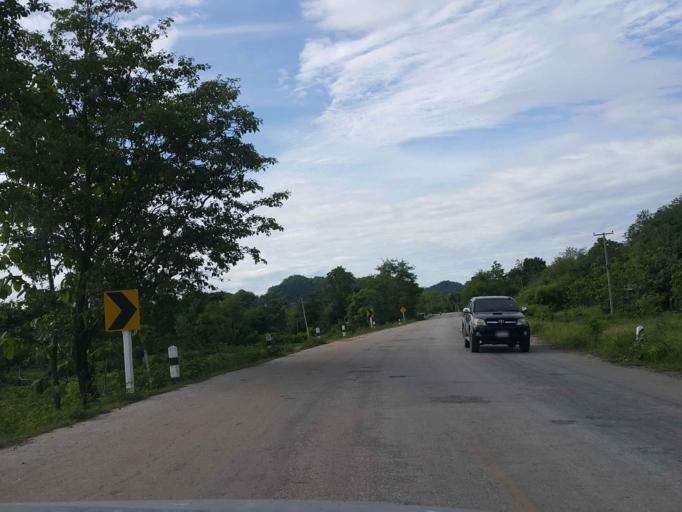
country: TH
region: Sukhothai
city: Thung Saliam
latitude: 17.2749
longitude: 99.5307
